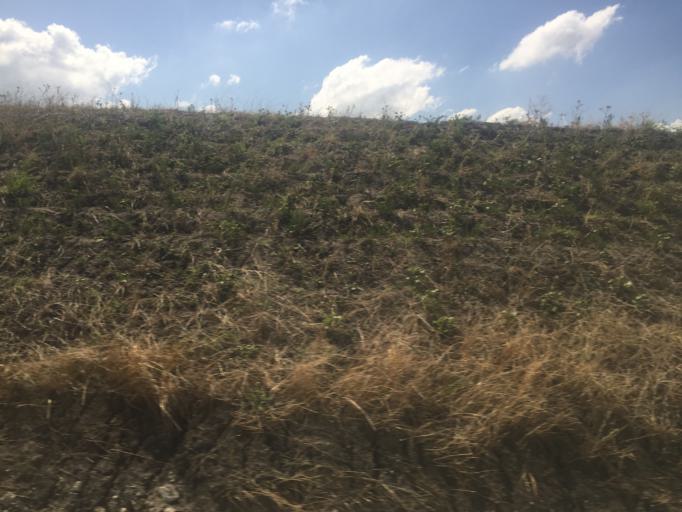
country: TR
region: Balikesir
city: Gobel
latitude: 39.9697
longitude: 28.1593
